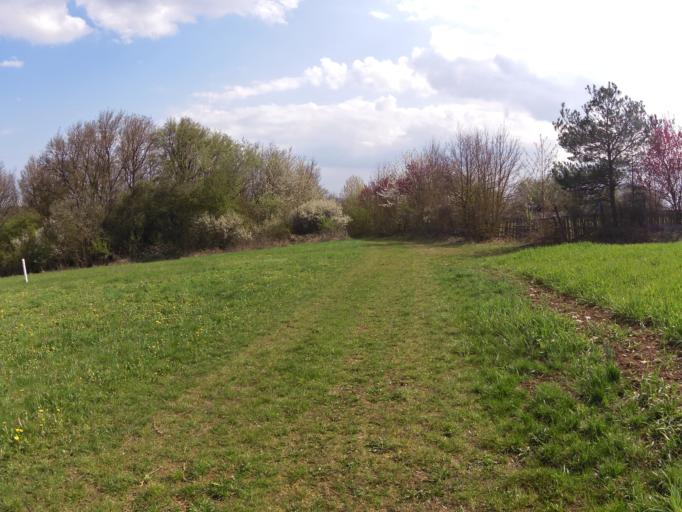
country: DE
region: Bavaria
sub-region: Regierungsbezirk Unterfranken
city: Rimpar
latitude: 49.8695
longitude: 9.9627
